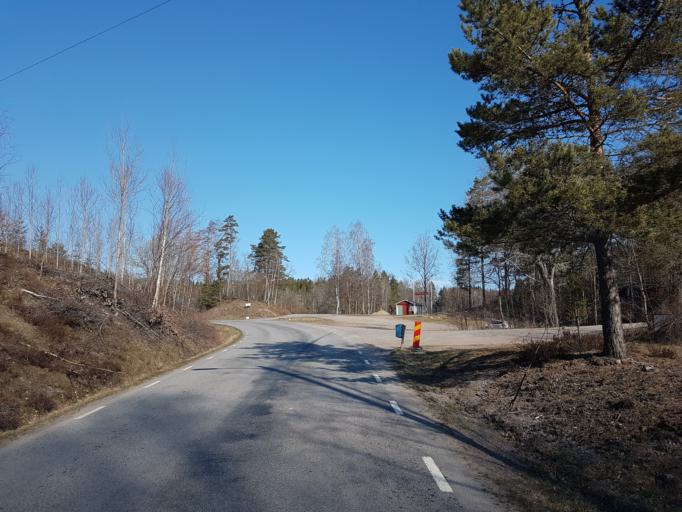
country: SE
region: OEstergoetland
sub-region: Valdemarsviks Kommun
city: Gusum
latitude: 58.1975
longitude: 16.3682
